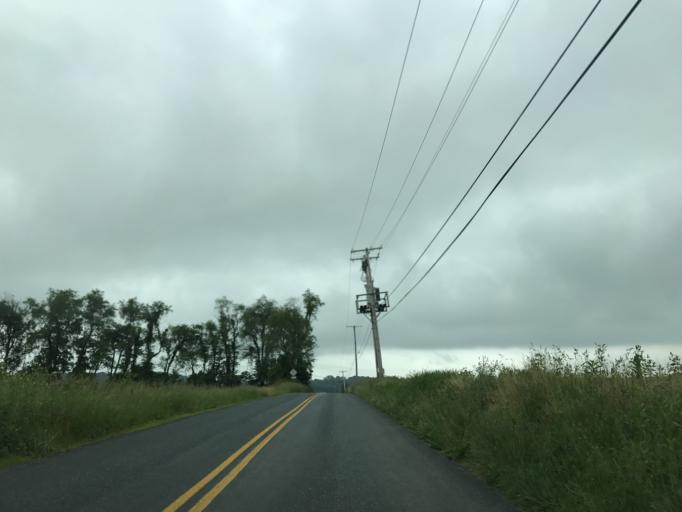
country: US
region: Maryland
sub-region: Harford County
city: Jarrettsville
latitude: 39.6963
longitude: -76.4510
